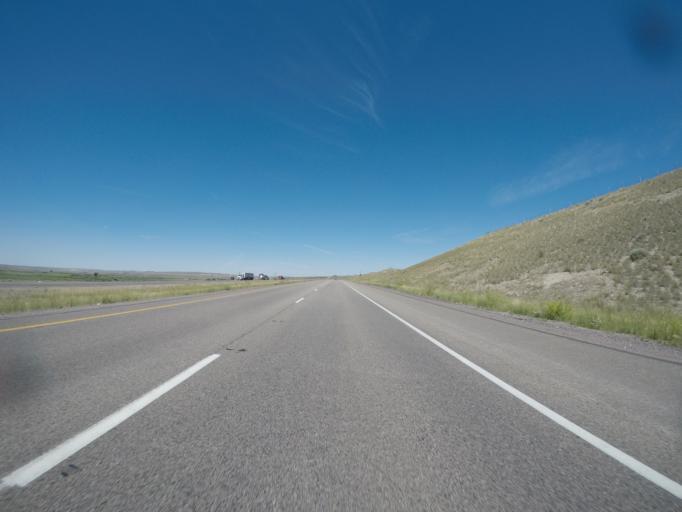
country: US
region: Wyoming
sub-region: Carbon County
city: Saratoga
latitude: 41.7407
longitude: -106.7598
